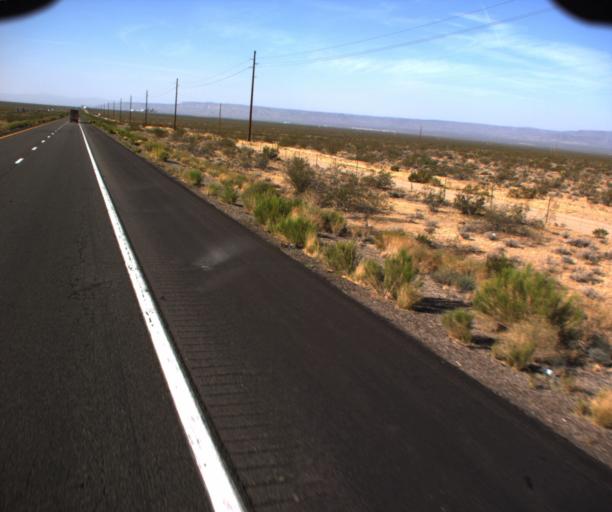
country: US
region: Arizona
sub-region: Mohave County
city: Kingman
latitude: 35.1003
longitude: -114.1183
